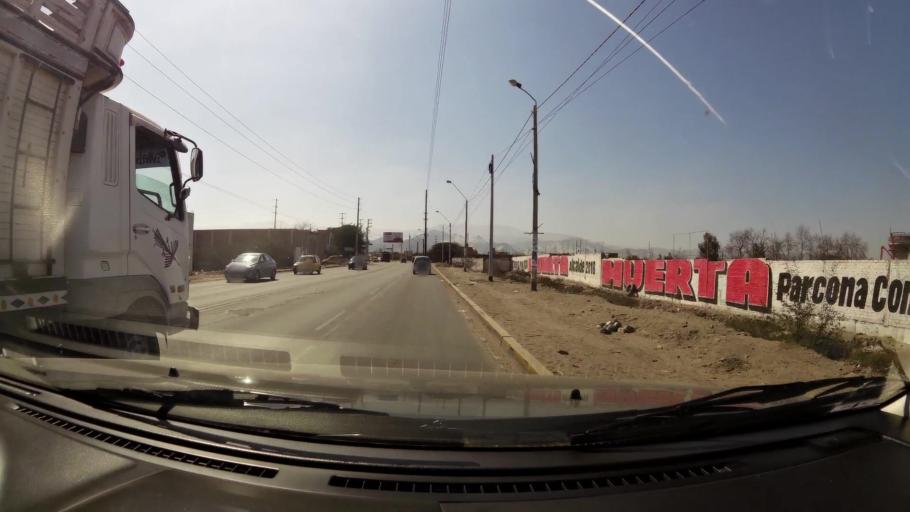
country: PE
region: Ica
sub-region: Provincia de Ica
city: Ica
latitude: -14.0587
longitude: -75.7119
